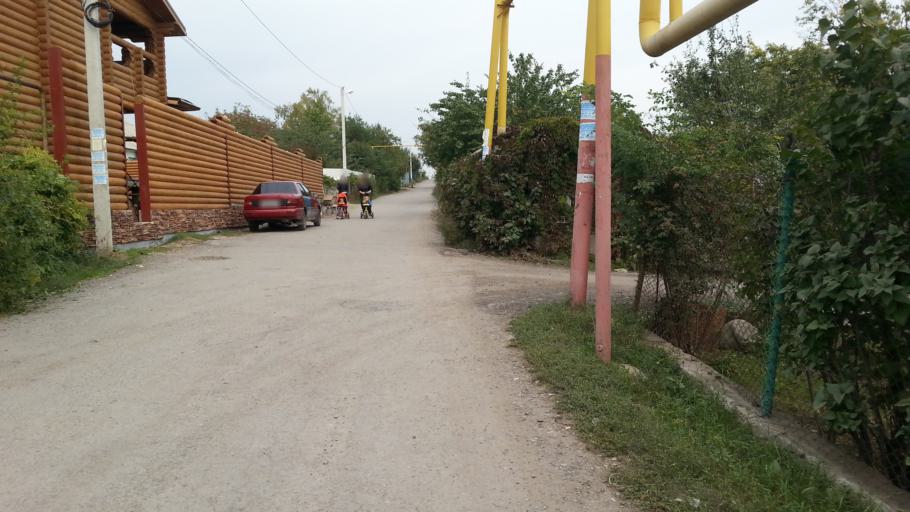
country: RU
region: Rostov
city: Severnyy
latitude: 47.2947
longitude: 39.6702
